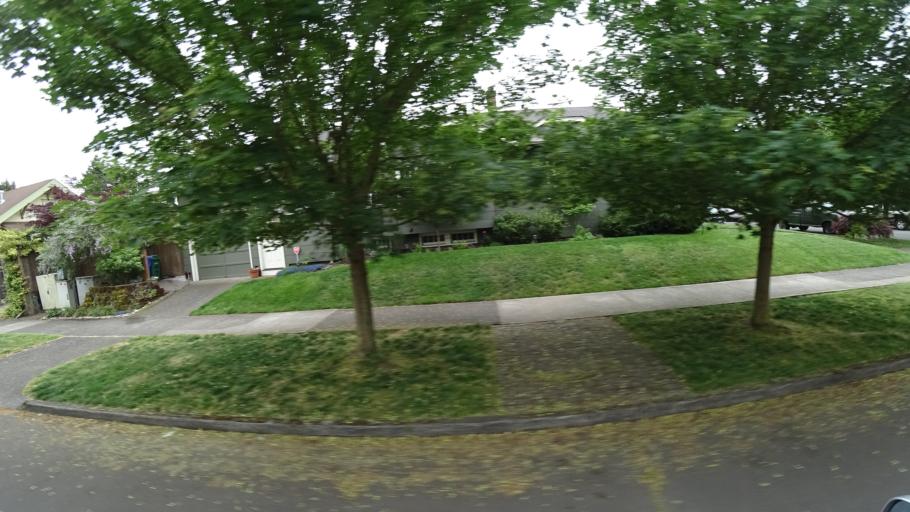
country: US
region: Oregon
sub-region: Multnomah County
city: Portland
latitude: 45.5437
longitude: -122.6114
